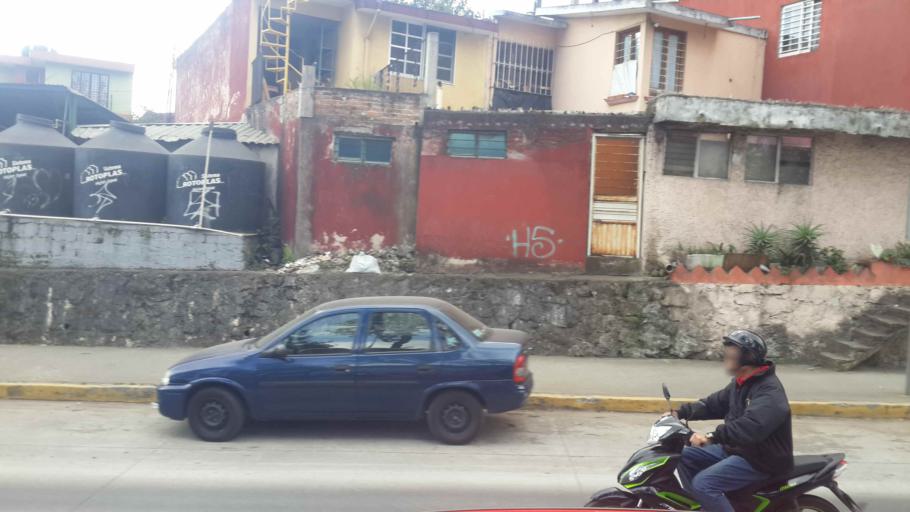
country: MX
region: Veracruz
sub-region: Xalapa
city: Xalapa de Enriquez
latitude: 19.5607
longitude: -96.9245
